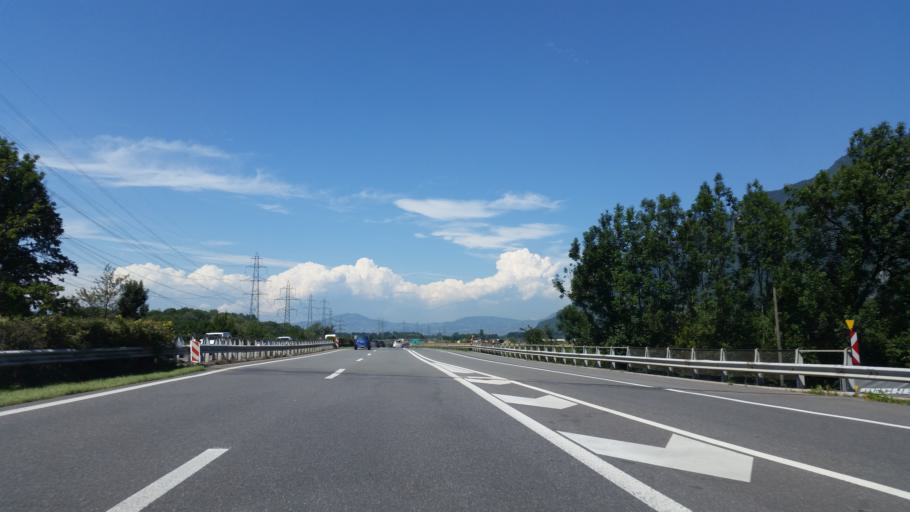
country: CH
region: Vaud
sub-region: Aigle District
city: Aigle
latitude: 46.3235
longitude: 6.9388
